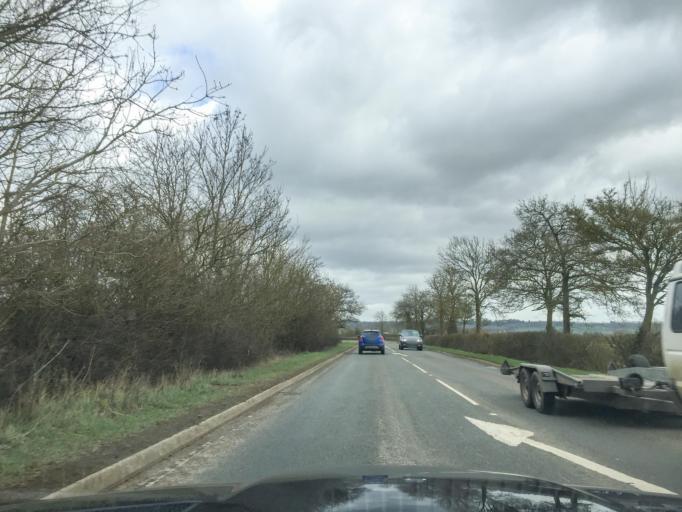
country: GB
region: England
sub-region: Warwickshire
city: Wellesbourne Mountford
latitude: 52.1234
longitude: -1.5395
